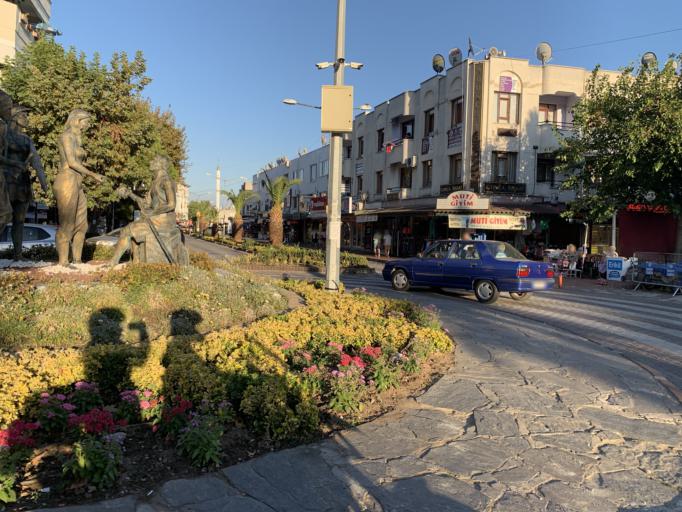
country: TR
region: Balikesir
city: Altinoluk
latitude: 39.5673
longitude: 26.7446
